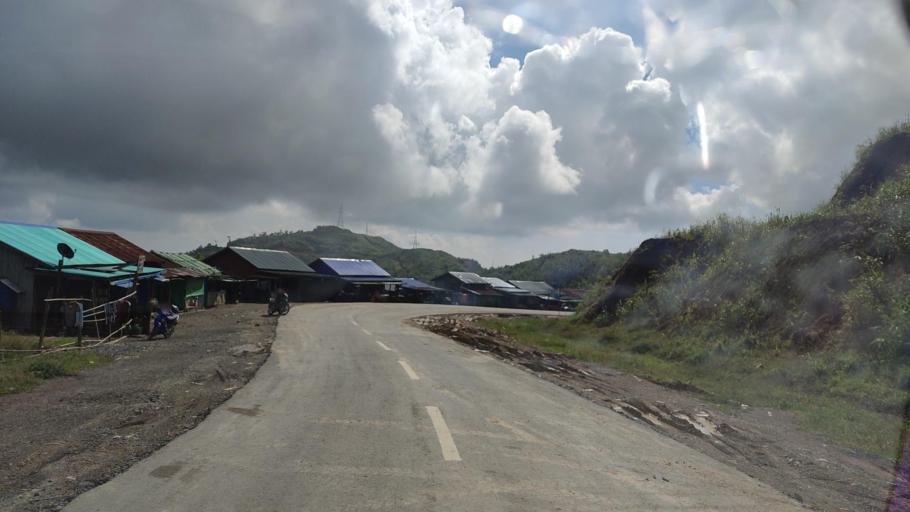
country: MM
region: Magway
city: Minbu
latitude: 19.8343
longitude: 94.2856
